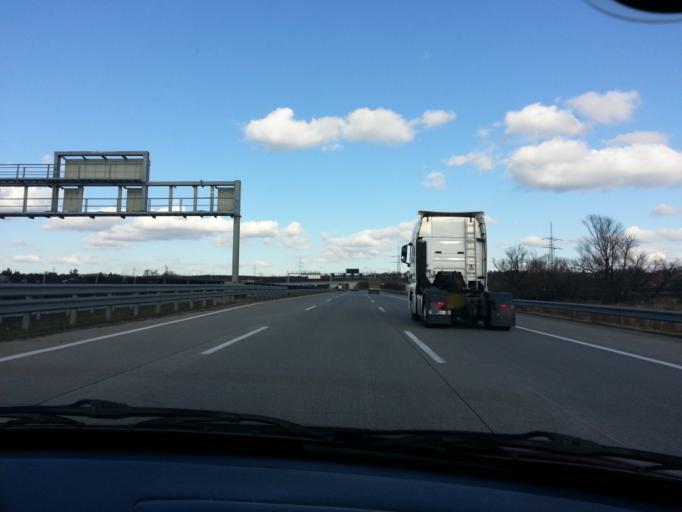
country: HU
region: Pest
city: Ecser
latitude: 47.4373
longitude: 19.3305
